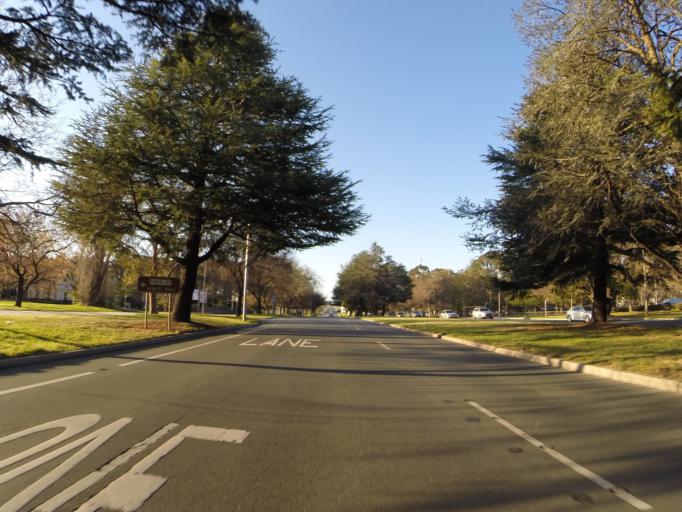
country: AU
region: Australian Capital Territory
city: Canberra
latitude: -35.2989
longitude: 149.1258
